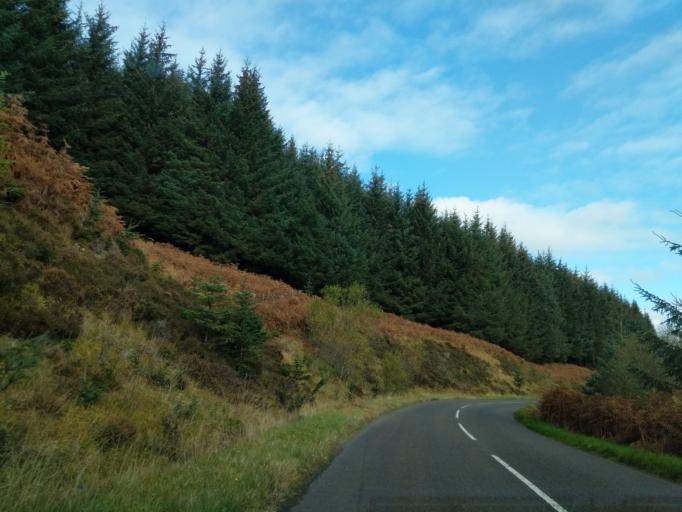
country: GB
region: Scotland
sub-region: Dumfries and Galloway
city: Castle Douglas
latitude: 55.1371
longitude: -4.0503
